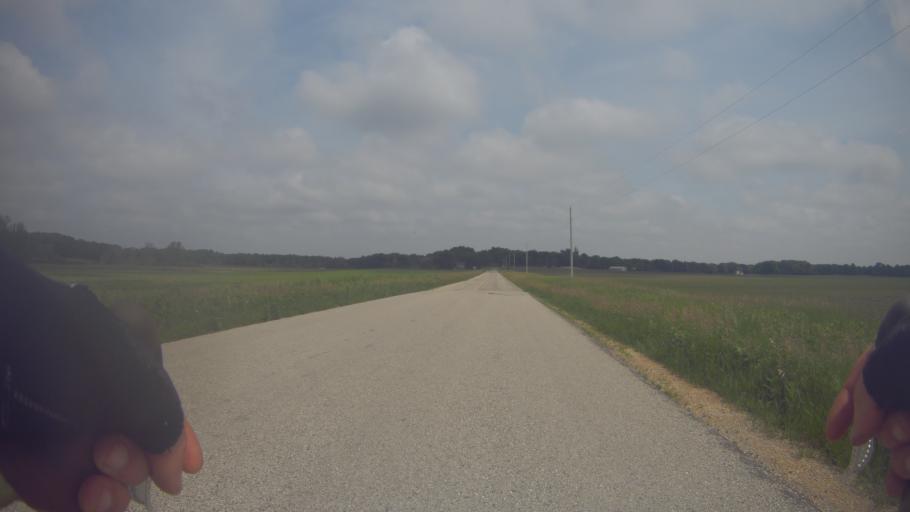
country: US
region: Wisconsin
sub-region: Jefferson County
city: Cambridge
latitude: 42.9246
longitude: -89.0039
